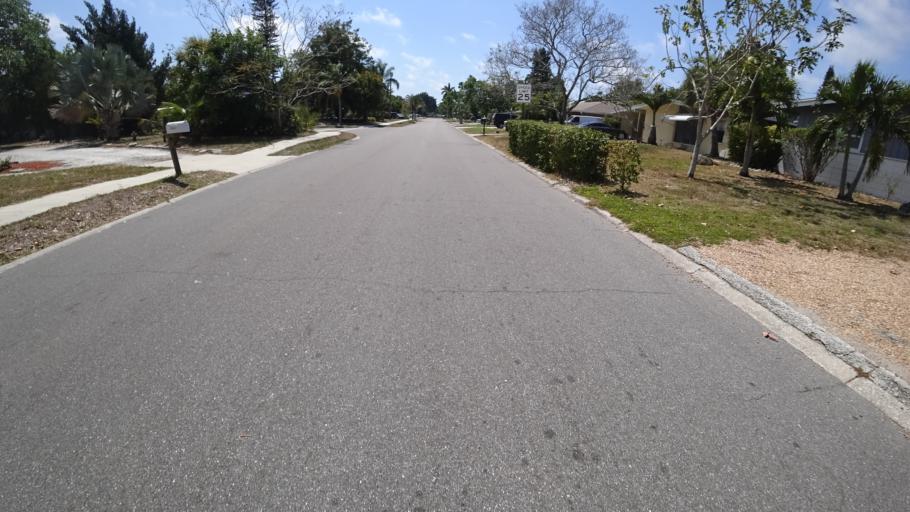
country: US
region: Florida
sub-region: Manatee County
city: Bayshore Gardens
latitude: 27.4310
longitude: -82.5813
